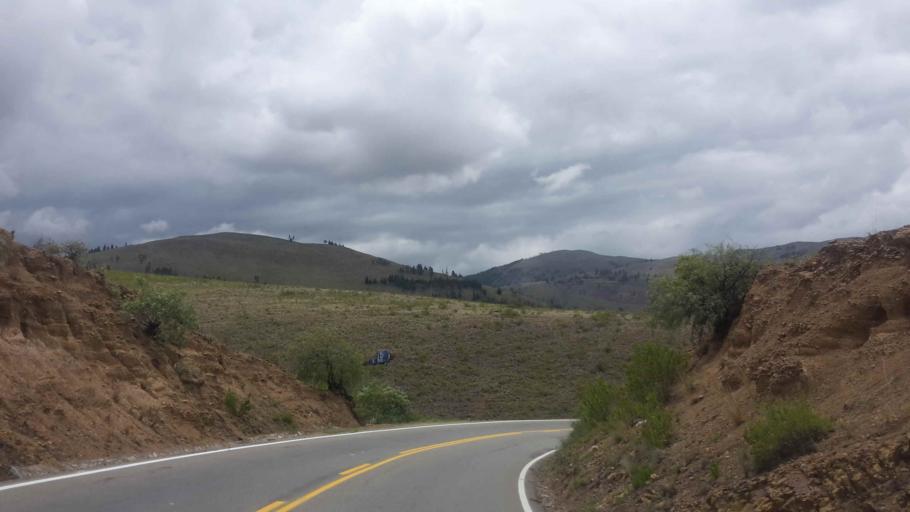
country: BO
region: Cochabamba
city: Arani
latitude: -17.4722
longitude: -65.7648
